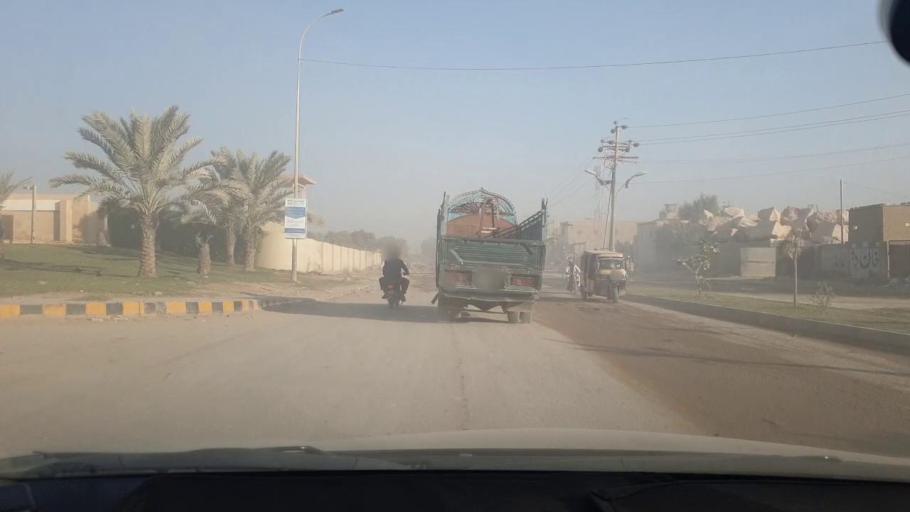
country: PK
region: Sindh
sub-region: Karachi District
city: Karachi
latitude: 24.9708
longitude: 67.0396
